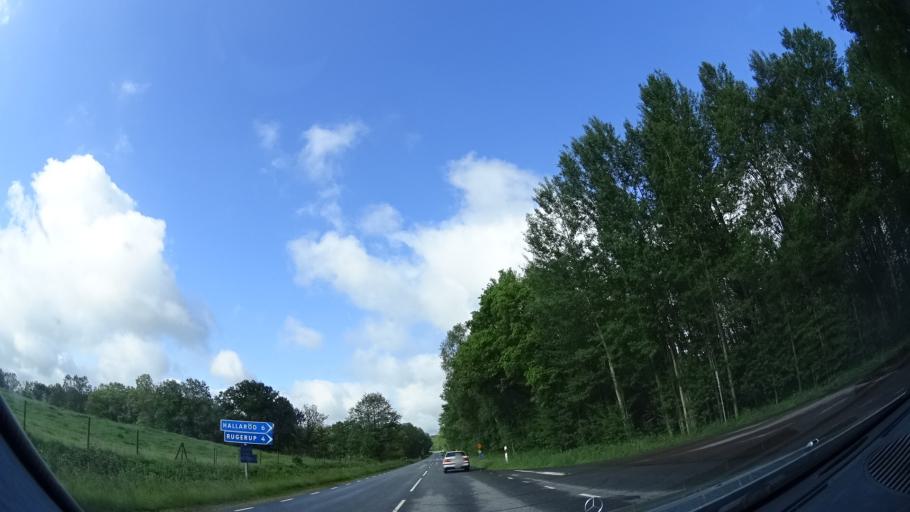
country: SE
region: Skane
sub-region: Eslovs Kommun
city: Stehag
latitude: 55.9418
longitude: 13.3965
